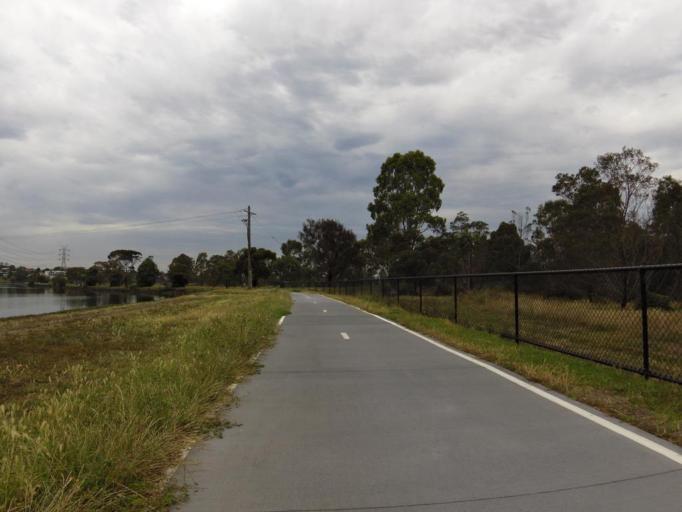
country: AU
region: Victoria
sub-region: Maribyrnong
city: Maribyrnong
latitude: -37.7796
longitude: 144.8967
